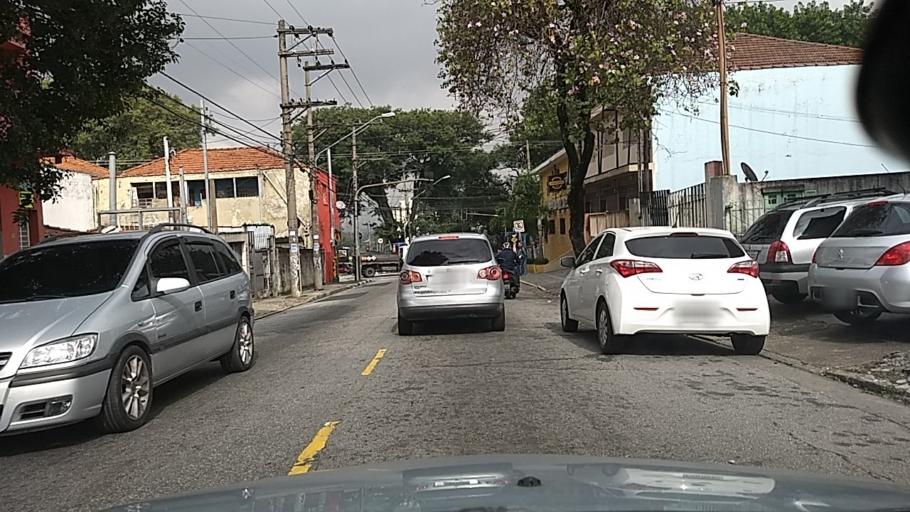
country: BR
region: Sao Paulo
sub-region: Sao Paulo
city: Sao Paulo
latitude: -23.5070
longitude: -46.5990
